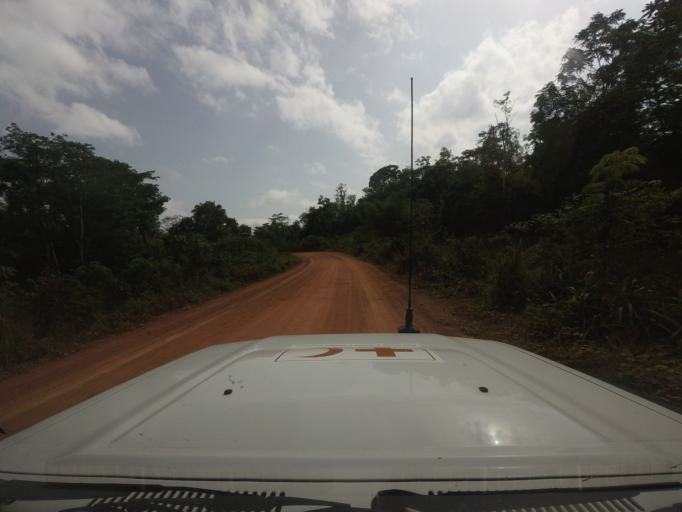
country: LR
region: Bong
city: Gbarnga
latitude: 7.2057
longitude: -9.4430
